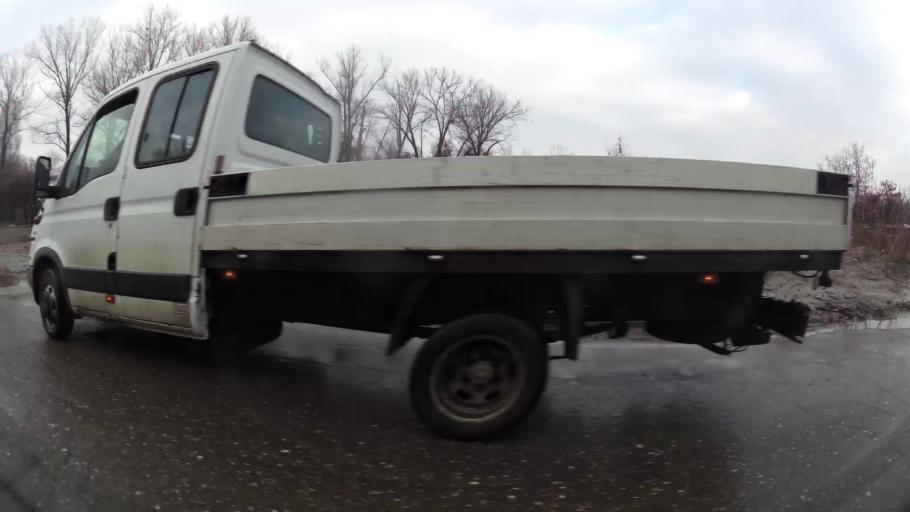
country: BG
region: Sofia-Capital
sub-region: Stolichna Obshtina
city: Sofia
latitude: 42.7196
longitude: 23.3615
